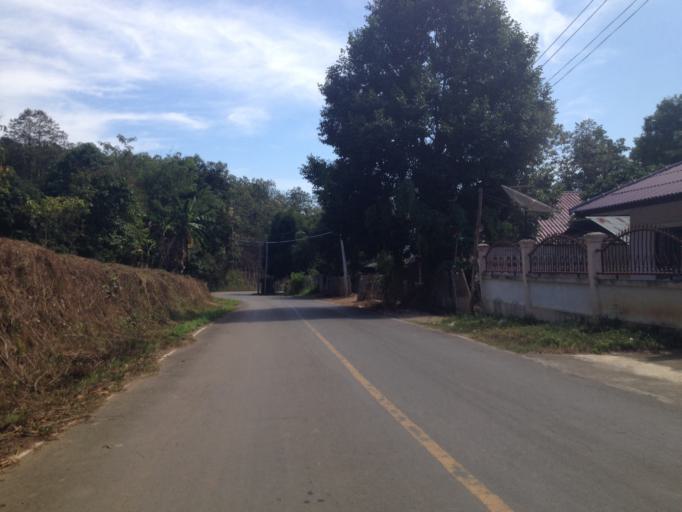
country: TH
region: Chiang Mai
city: Hang Dong
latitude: 18.7145
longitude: 98.8953
